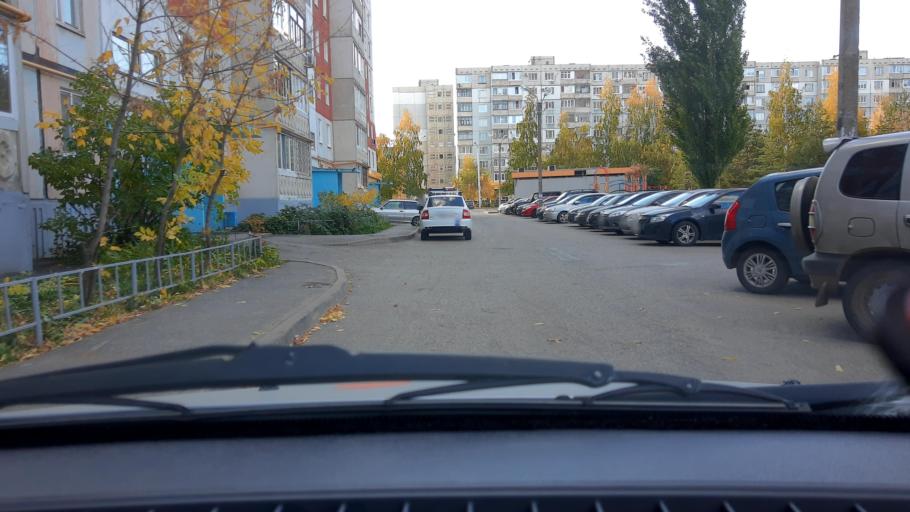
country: RU
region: Bashkortostan
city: Ufa
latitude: 54.7715
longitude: 56.0788
